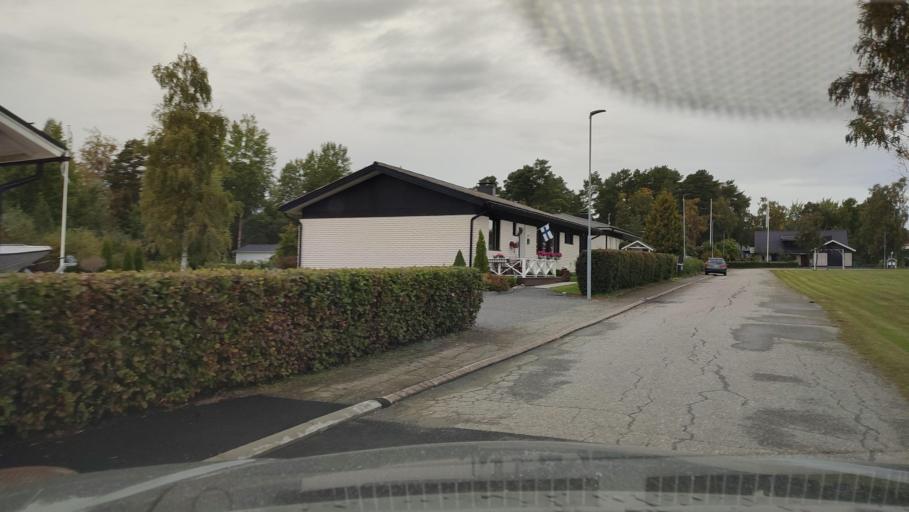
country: FI
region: Ostrobothnia
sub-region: Sydosterbotten
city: Kristinestad
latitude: 62.2817
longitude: 21.3618
